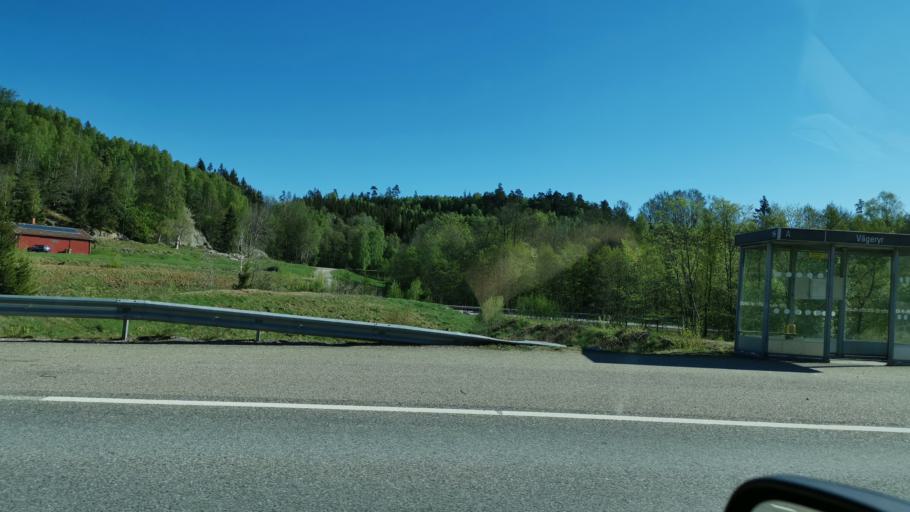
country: SE
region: Vaestra Goetaland
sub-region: Uddevalla Kommun
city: Ljungskile
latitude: 58.2624
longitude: 11.9002
